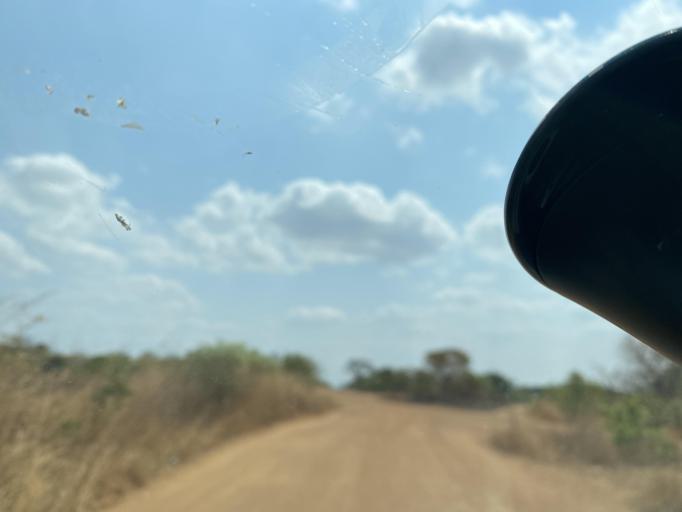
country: ZM
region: Lusaka
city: Chongwe
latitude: -15.5900
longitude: 28.7999
